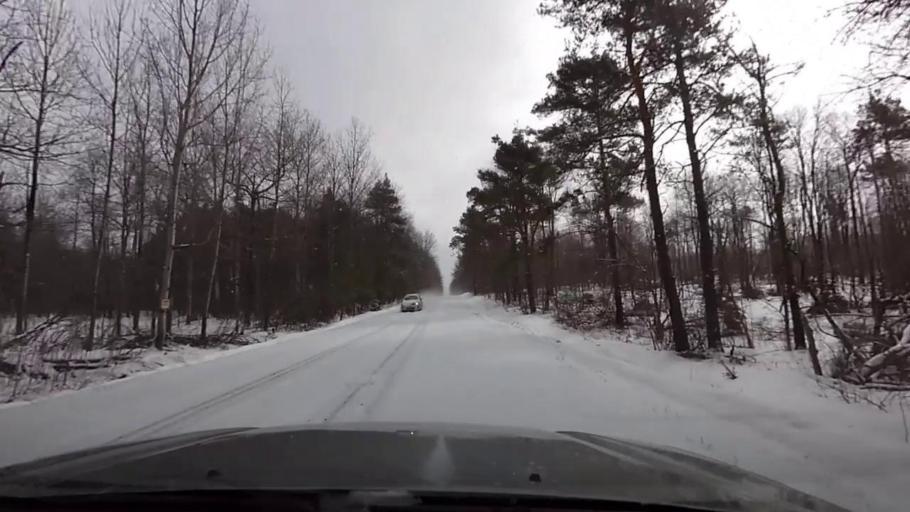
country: US
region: New York
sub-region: Cattaraugus County
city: Franklinville
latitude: 42.3380
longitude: -78.3605
